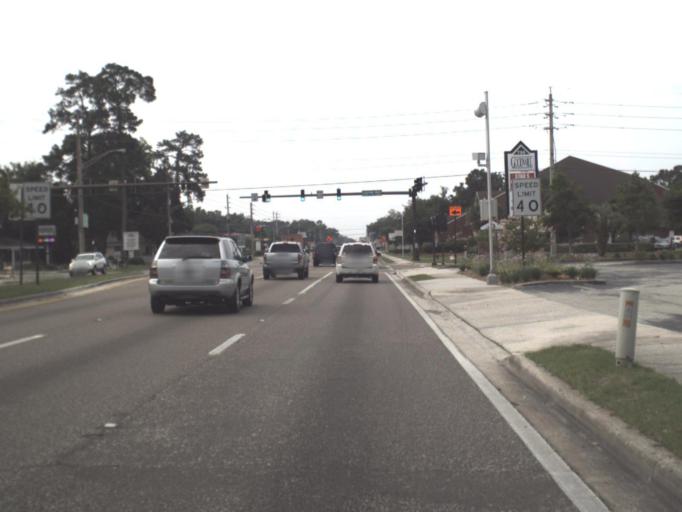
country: US
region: Florida
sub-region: Clay County
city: Orange Park
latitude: 30.1812
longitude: -81.7018
